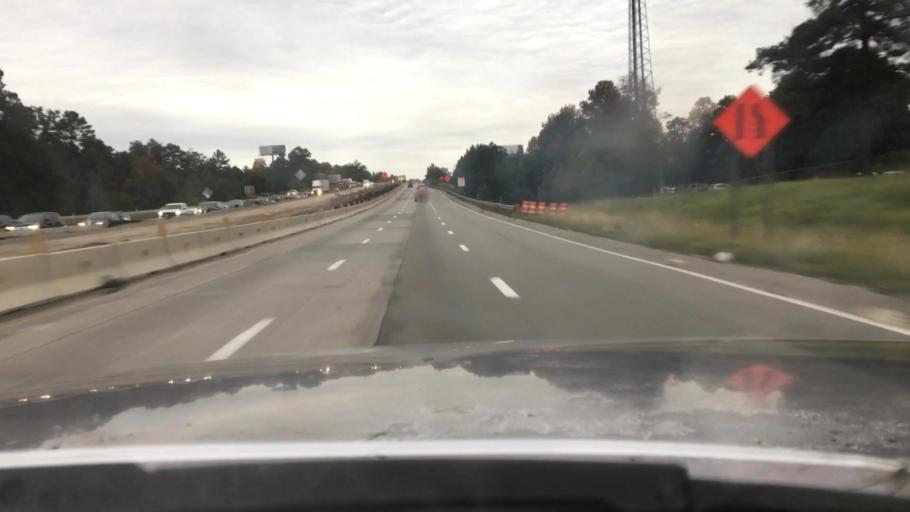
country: US
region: South Carolina
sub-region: Lexington County
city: Lexington
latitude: 33.9769
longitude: -81.1957
